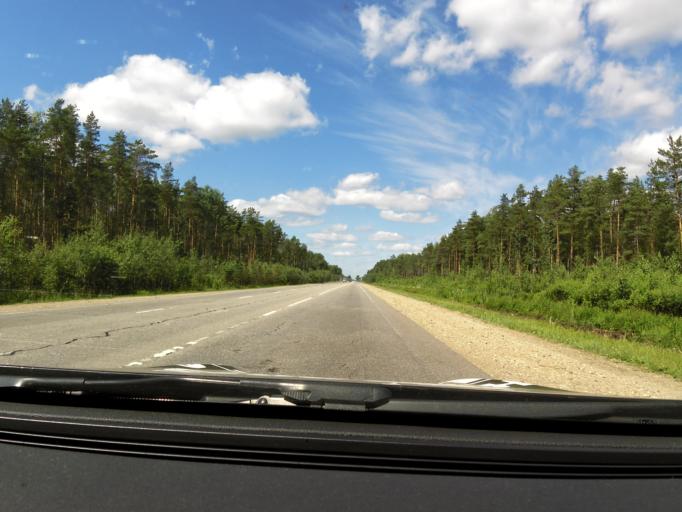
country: RU
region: Tverskaya
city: Kuzhenkino
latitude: 57.8011
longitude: 33.8660
